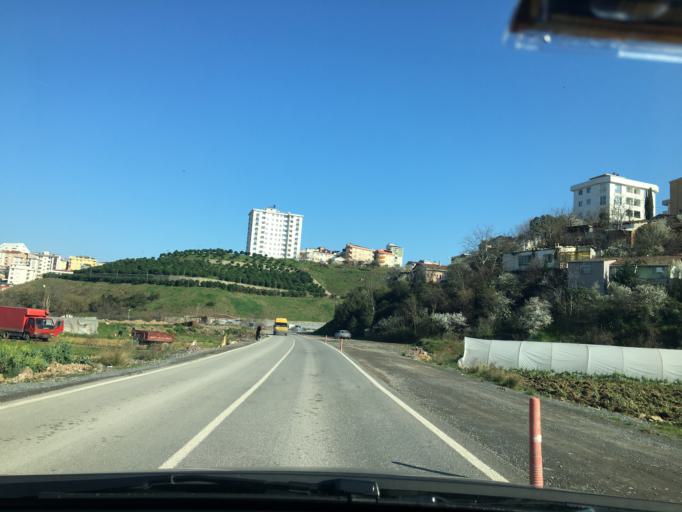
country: TR
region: Istanbul
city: Pendik
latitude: 40.8729
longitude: 29.2991
